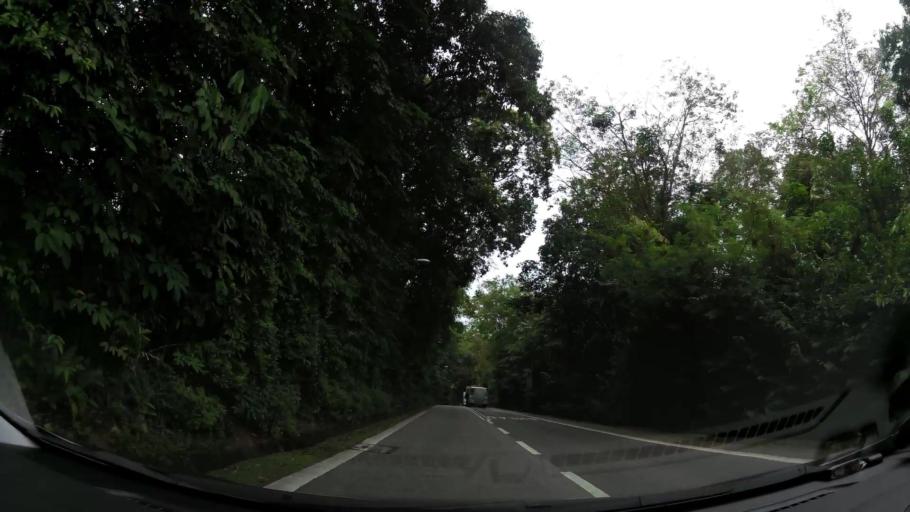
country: MY
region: Johor
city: Kampung Pasir Gudang Baru
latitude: 1.4108
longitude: 103.9091
